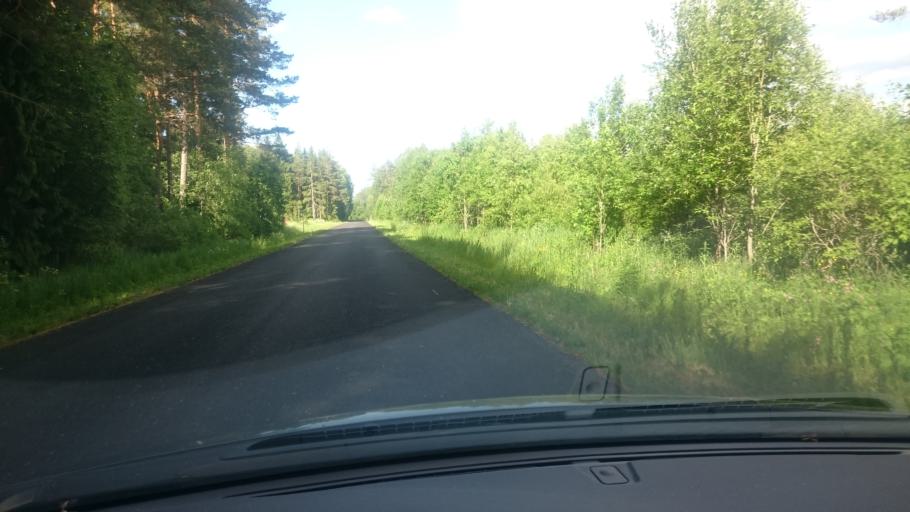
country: EE
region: Harju
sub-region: Rae vald
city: Vaida
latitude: 59.2295
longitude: 25.0120
